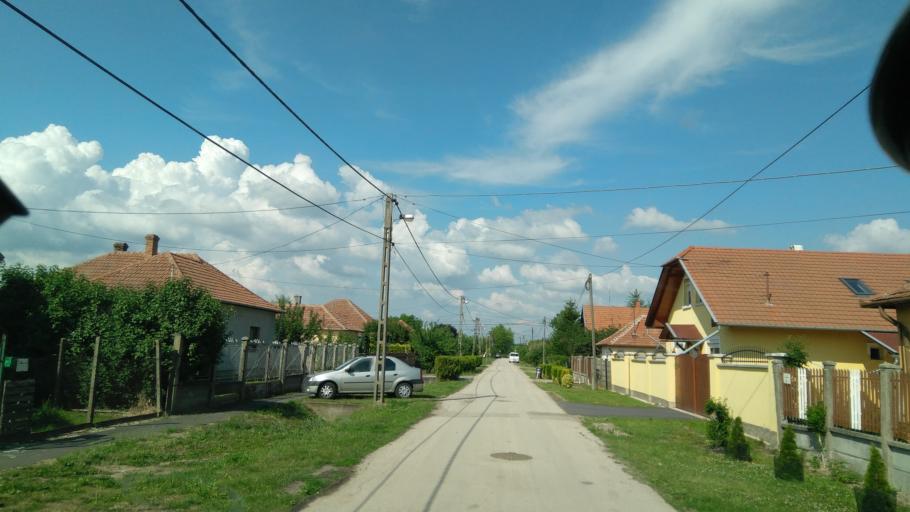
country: HU
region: Bekes
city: Doboz
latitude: 46.7026
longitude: 21.1787
